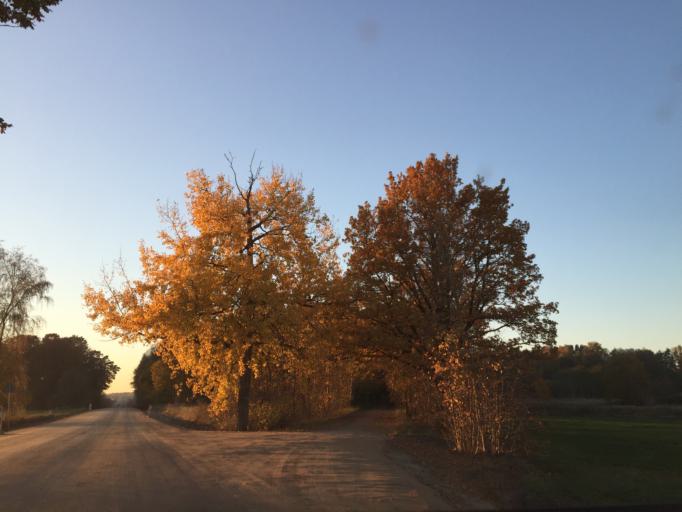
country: LT
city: Vieksniai
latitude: 56.4056
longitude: 22.5158
